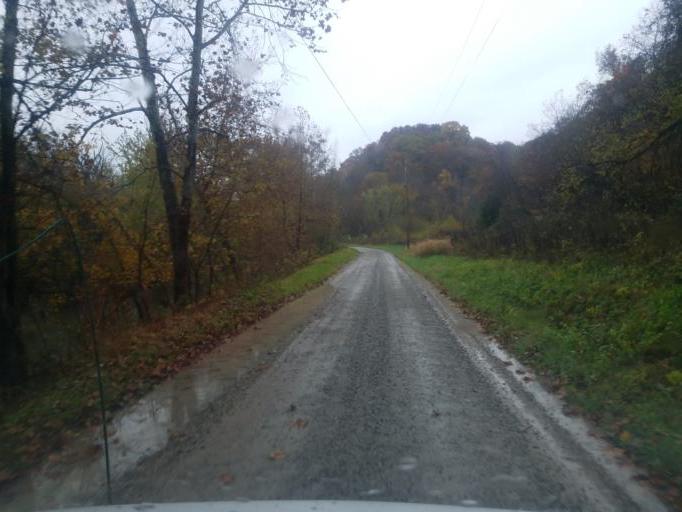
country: US
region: Ohio
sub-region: Washington County
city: Beverly
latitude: 39.4794
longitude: -81.7417
